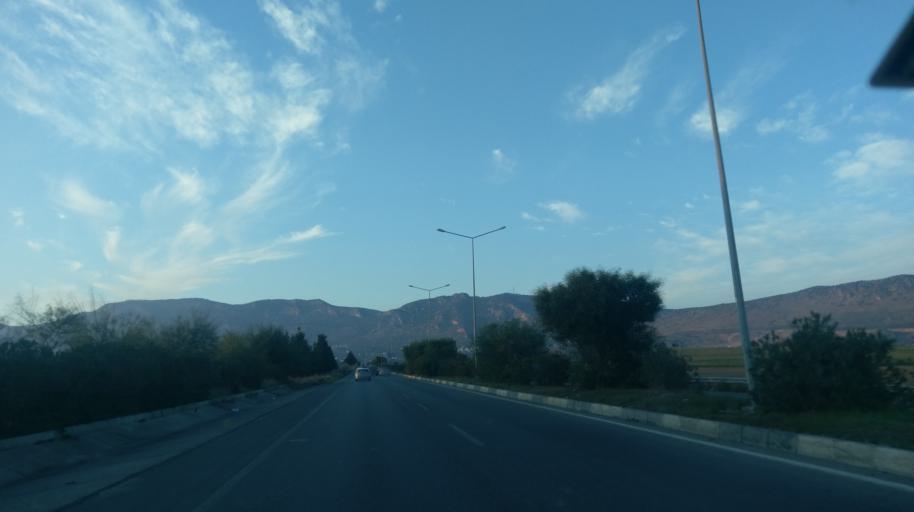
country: CY
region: Keryneia
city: Kyrenia
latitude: 35.2626
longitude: 33.2953
